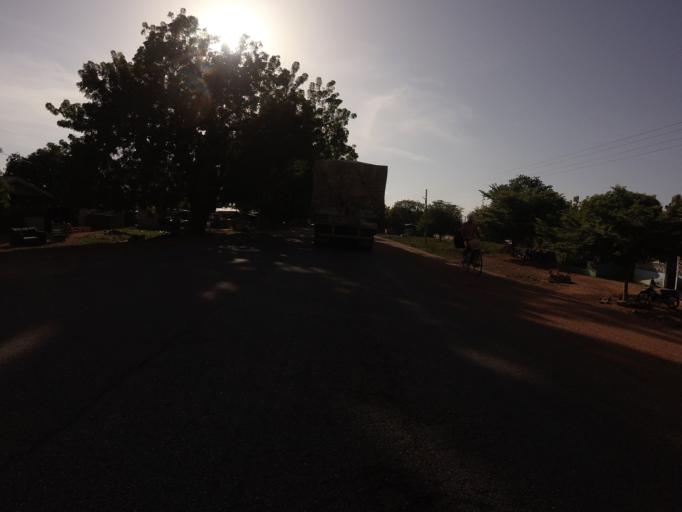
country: GH
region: Upper East
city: Navrongo
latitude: 10.8932
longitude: -1.0815
